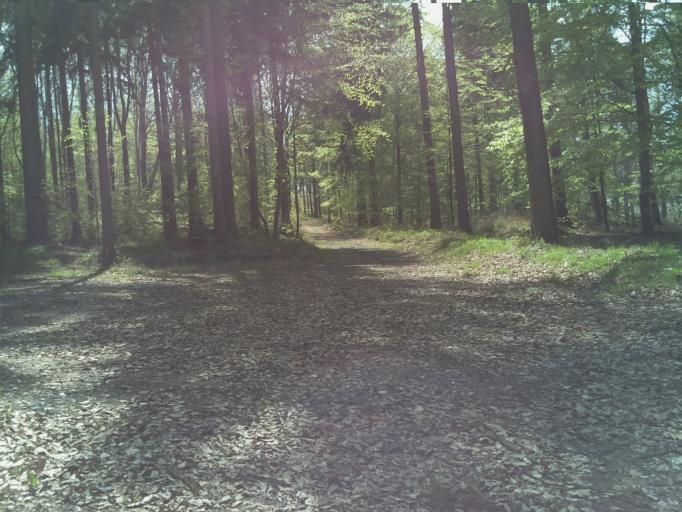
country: PL
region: Lower Silesian Voivodeship
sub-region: Powiat swidnicki
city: Swiebodzice
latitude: 50.8195
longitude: 16.3205
